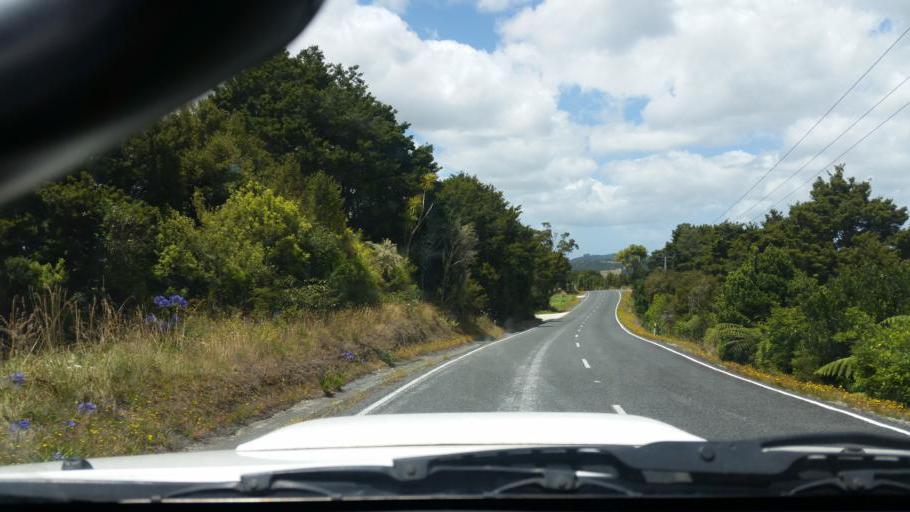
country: NZ
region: Northland
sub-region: Whangarei
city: Ruakaka
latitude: -36.0651
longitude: 174.2668
